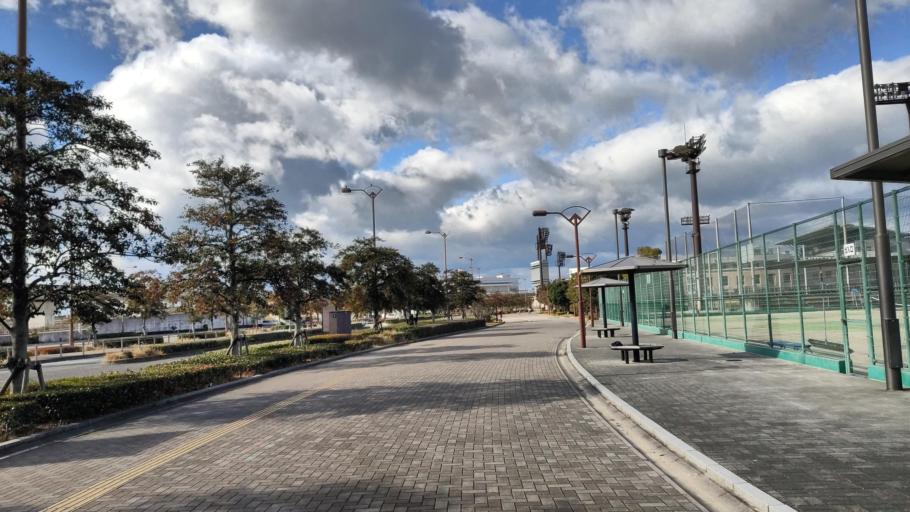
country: JP
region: Ehime
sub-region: Shikoku-chuo Shi
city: Matsuyama
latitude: 33.8076
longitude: 132.7459
